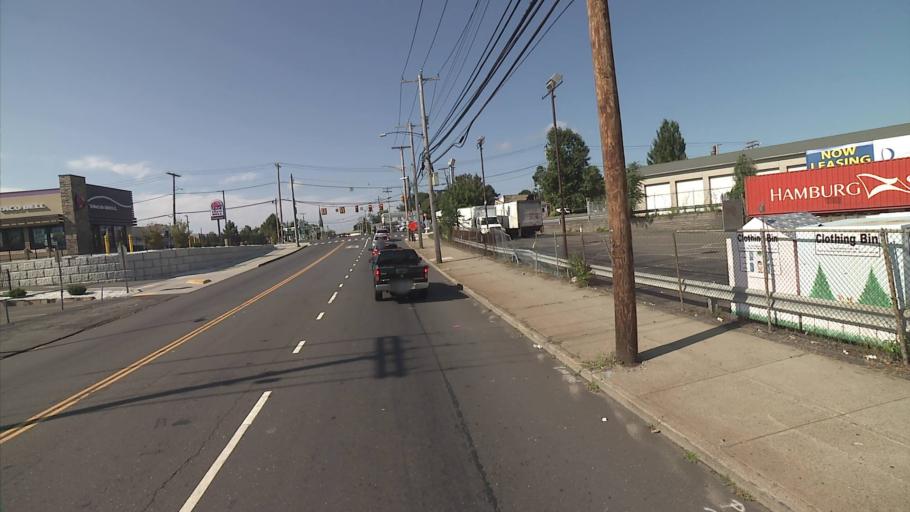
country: US
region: Connecticut
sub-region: Fairfield County
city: Bridgeport
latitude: 41.1974
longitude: -73.1928
